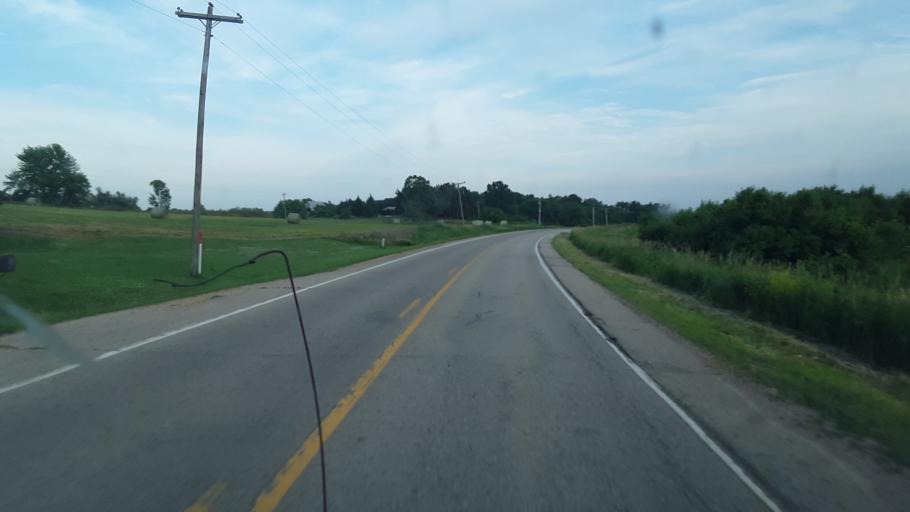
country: US
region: Iowa
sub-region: Benton County
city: Belle Plaine
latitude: 41.9479
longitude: -92.4177
